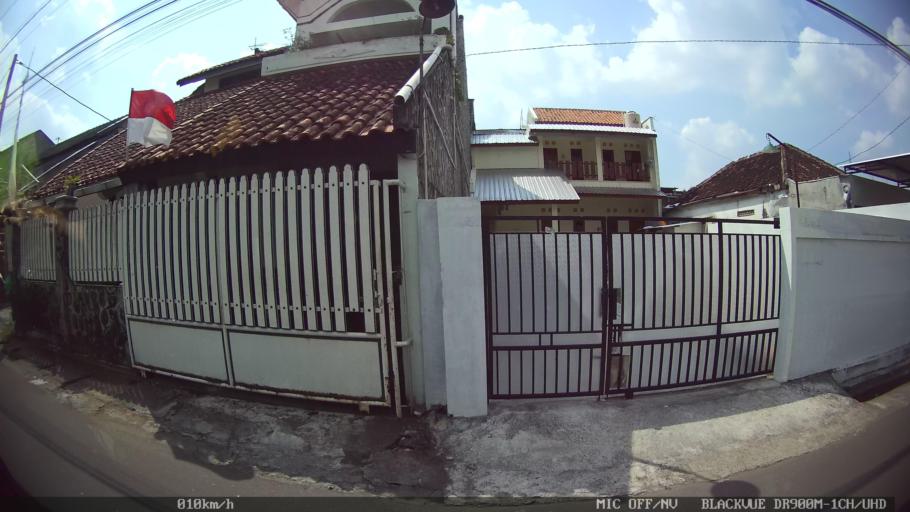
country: ID
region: Daerah Istimewa Yogyakarta
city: Yogyakarta
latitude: -7.8075
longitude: 110.4036
